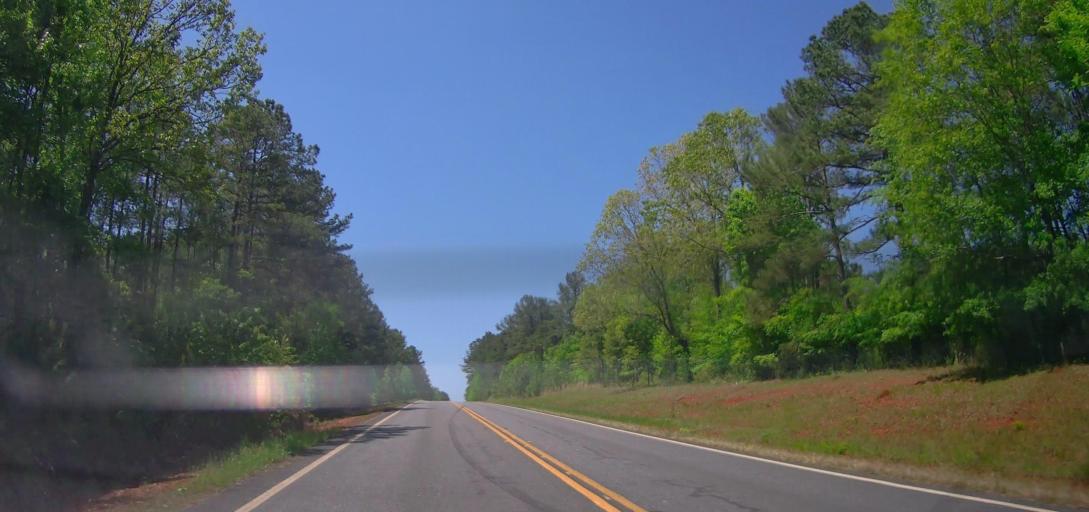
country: US
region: Georgia
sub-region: Putnam County
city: Eatonton
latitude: 33.2133
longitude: -83.4819
